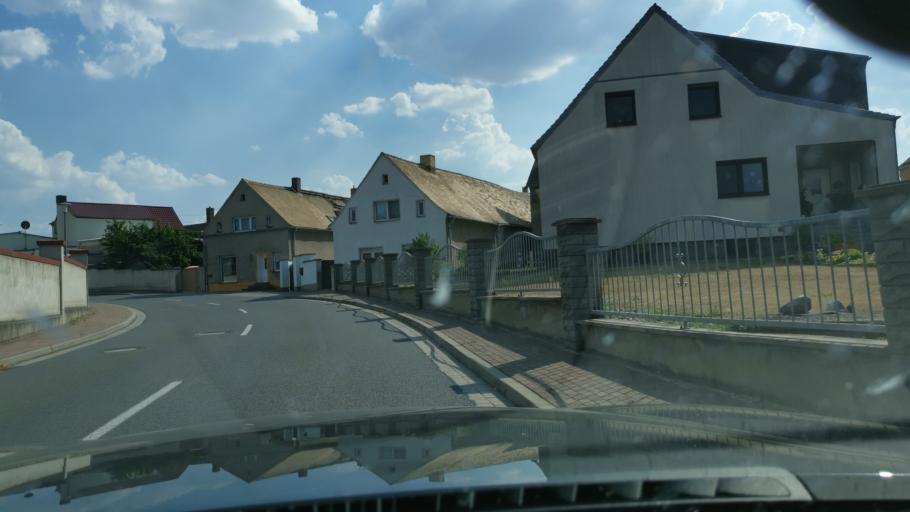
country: DE
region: Saxony
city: Zschepplin
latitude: 51.5328
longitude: 12.5960
